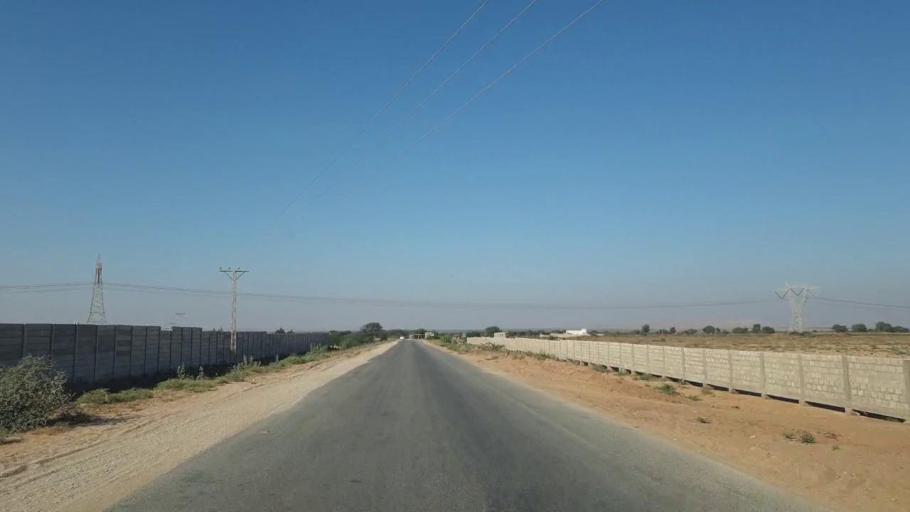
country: PK
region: Sindh
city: Gharo
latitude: 25.1868
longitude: 67.6571
